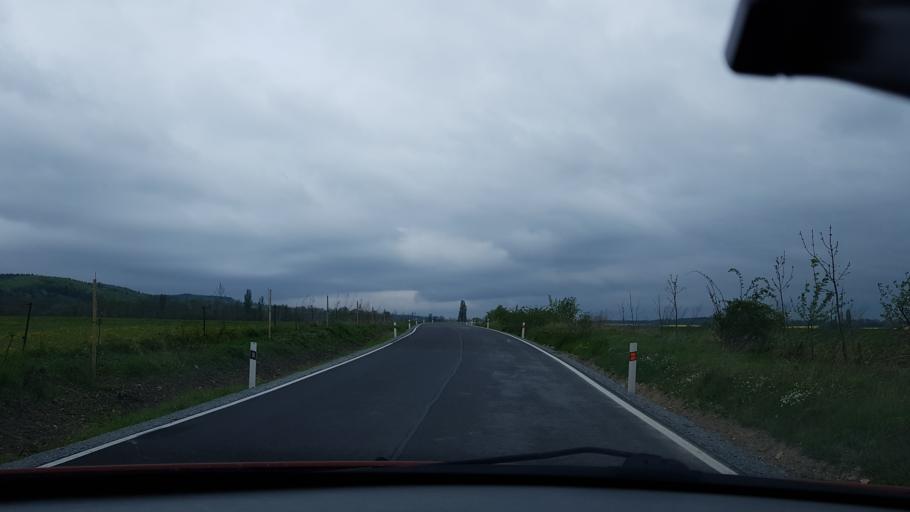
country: PL
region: Opole Voivodeship
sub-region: Powiat nyski
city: Kamienica
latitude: 50.4343
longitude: 16.9446
